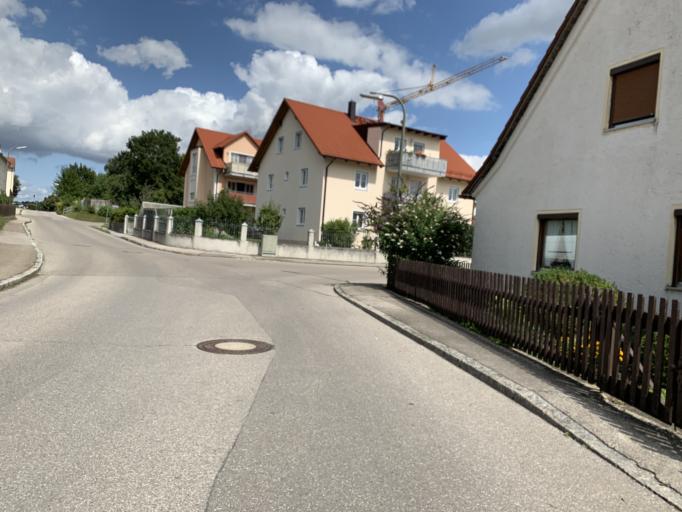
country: DE
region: Bavaria
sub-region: Upper Bavaria
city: Zolling
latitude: 48.4501
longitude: 11.7744
